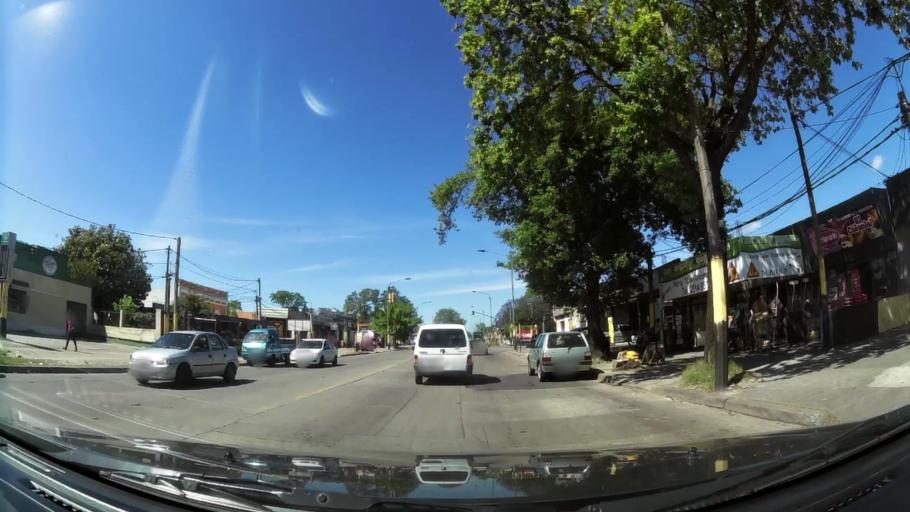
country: UY
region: Canelones
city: Paso de Carrasco
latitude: -34.8454
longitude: -56.1257
